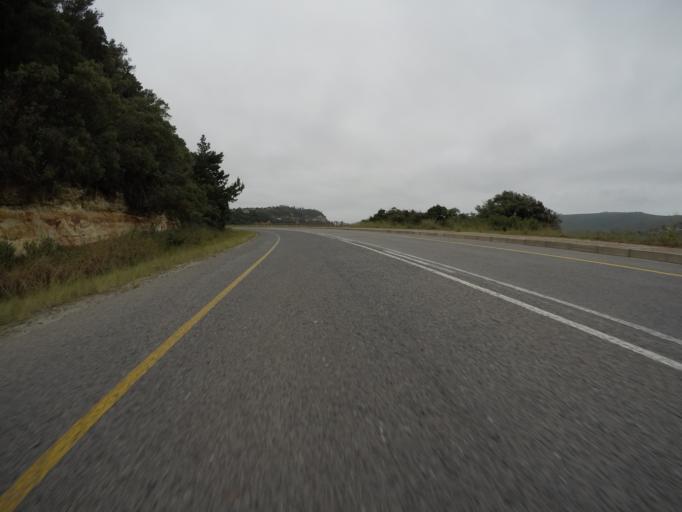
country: ZA
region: Western Cape
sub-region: Eden District Municipality
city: Knysna
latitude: -34.0285
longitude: 23.0007
